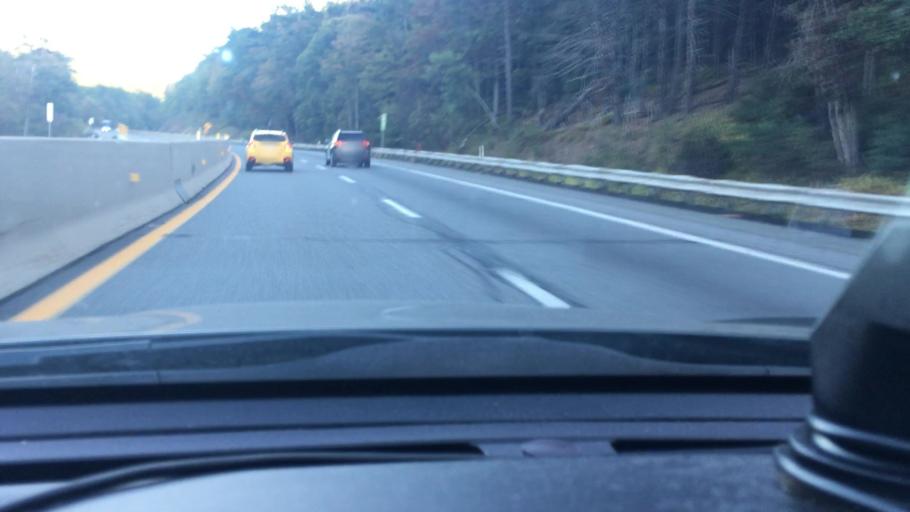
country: US
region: Pennsylvania
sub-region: Carbon County
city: Weissport East
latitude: 40.9133
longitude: -75.6463
